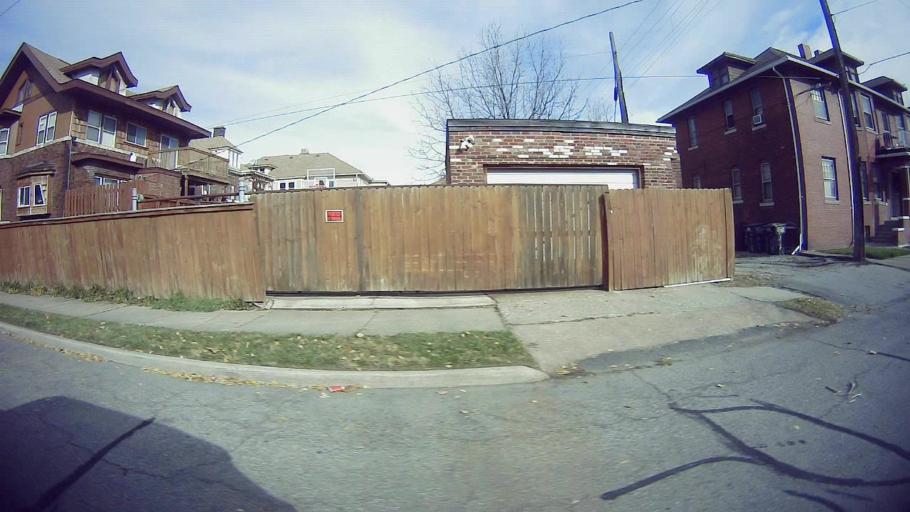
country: US
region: Michigan
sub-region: Wayne County
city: Highland Park
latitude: 42.3821
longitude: -83.0849
